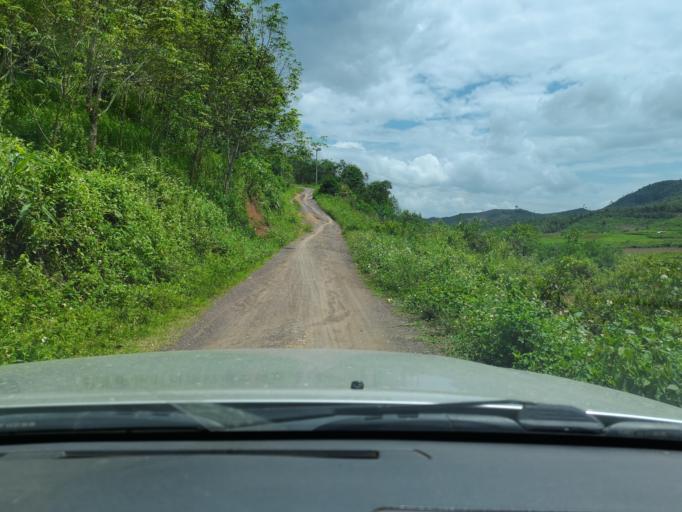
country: LA
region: Loungnamtha
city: Muang Long
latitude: 20.7204
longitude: 101.0139
